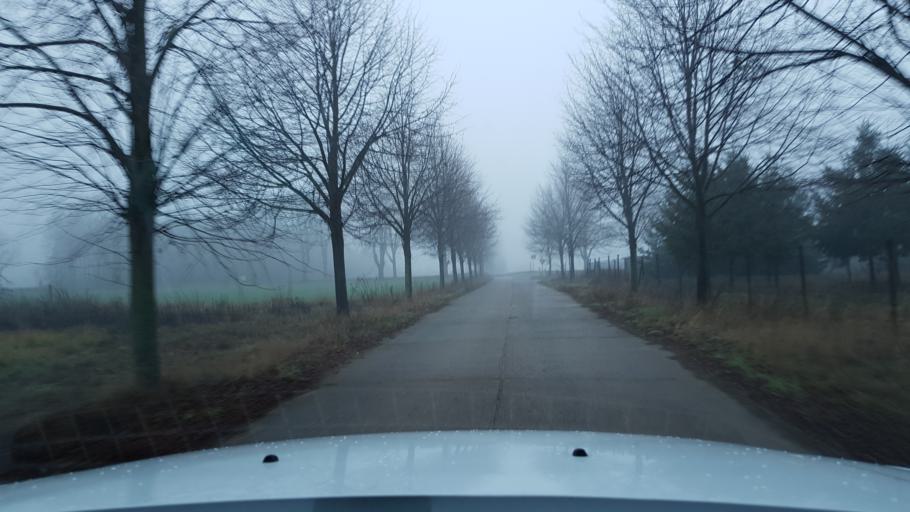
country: DE
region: Brandenburg
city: Mescherin
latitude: 53.2836
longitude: 14.4085
